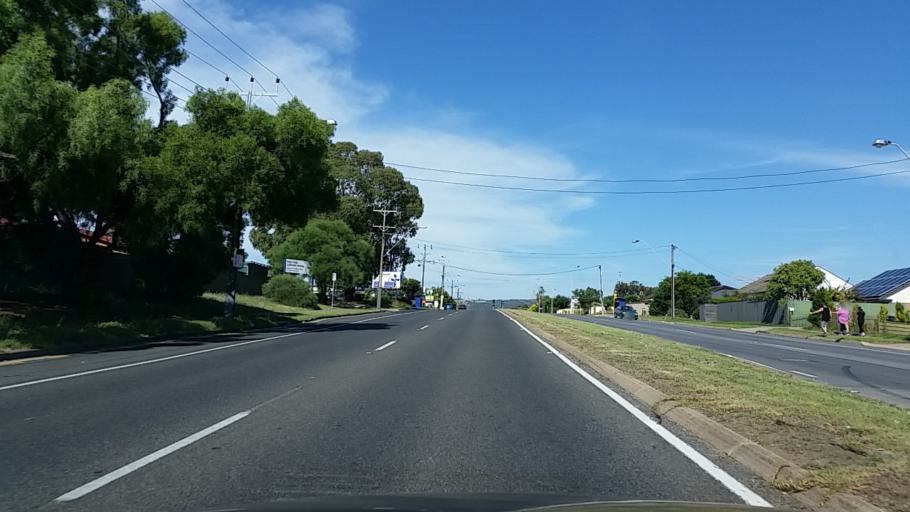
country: AU
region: South Australia
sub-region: Tea Tree Gully
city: Modbury
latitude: -34.8294
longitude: 138.6658
